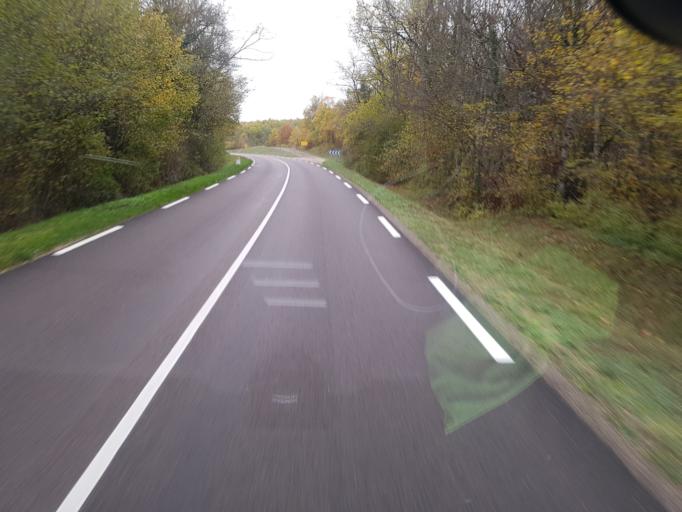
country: FR
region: Bourgogne
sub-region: Departement de la Cote-d'Or
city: Is-sur-Tille
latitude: 47.5229
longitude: 5.0013
